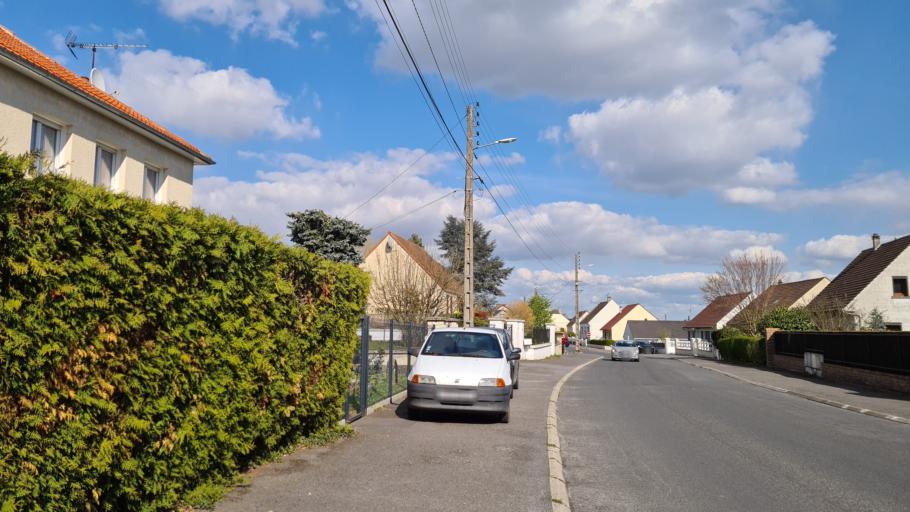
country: FR
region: Picardie
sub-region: Departement de l'Aisne
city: Laon
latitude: 49.5581
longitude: 3.6247
